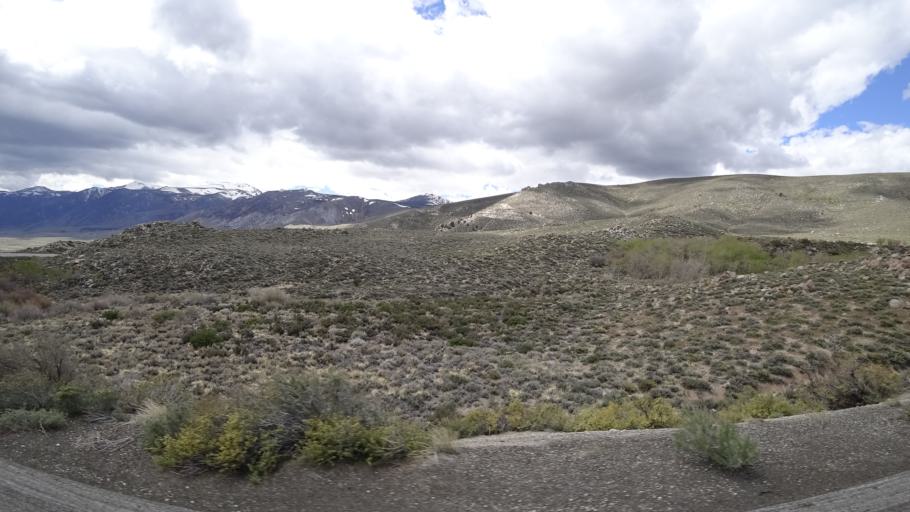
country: US
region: California
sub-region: Mono County
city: Bridgeport
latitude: 38.0835
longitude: -119.1587
